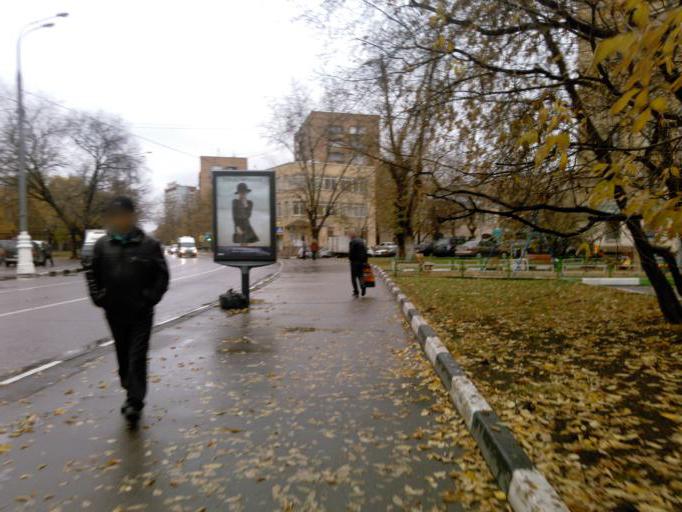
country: RU
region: Moscow
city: Zamoskvorech'ye
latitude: 55.7100
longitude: 37.6193
